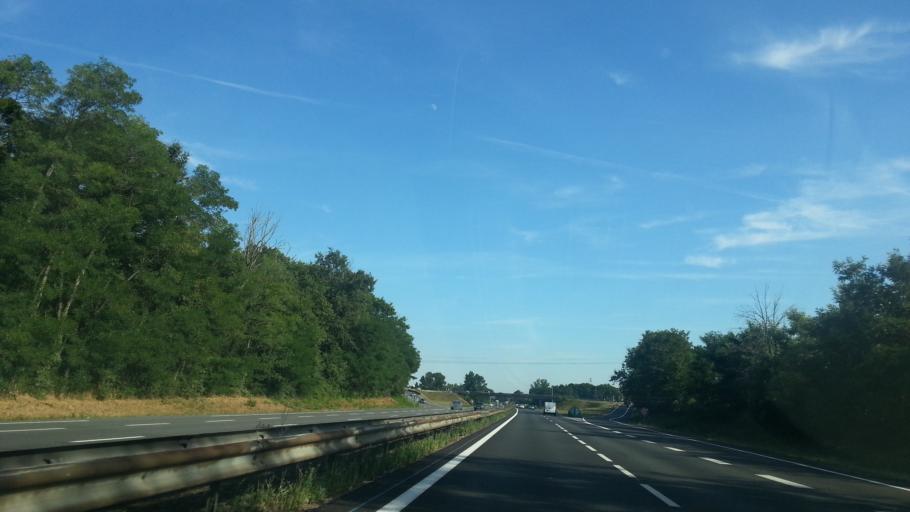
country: FR
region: Aquitaine
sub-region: Departement de la Gironde
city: Martillac
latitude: 44.7280
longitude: -0.5283
